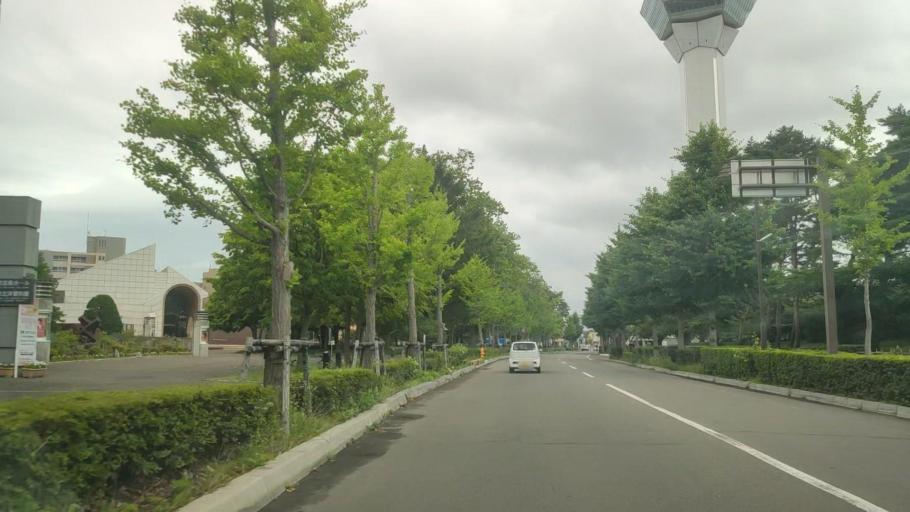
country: JP
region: Hokkaido
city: Hakodate
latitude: 41.7940
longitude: 140.7560
